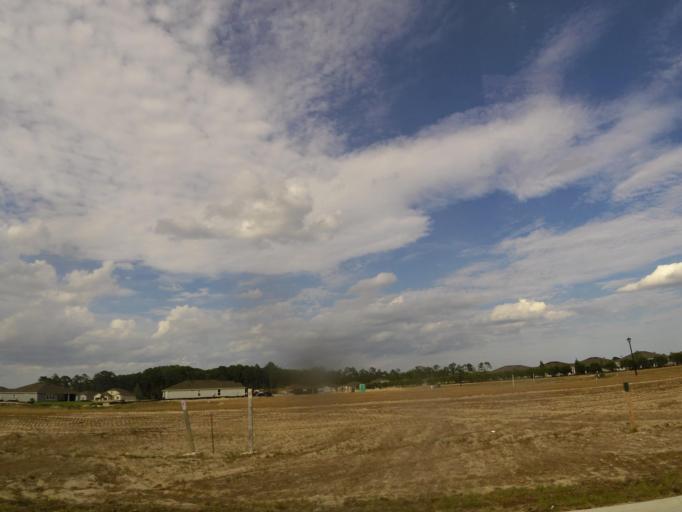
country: US
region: Florida
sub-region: Saint Johns County
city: Palm Valley
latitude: 30.1761
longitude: -81.5113
